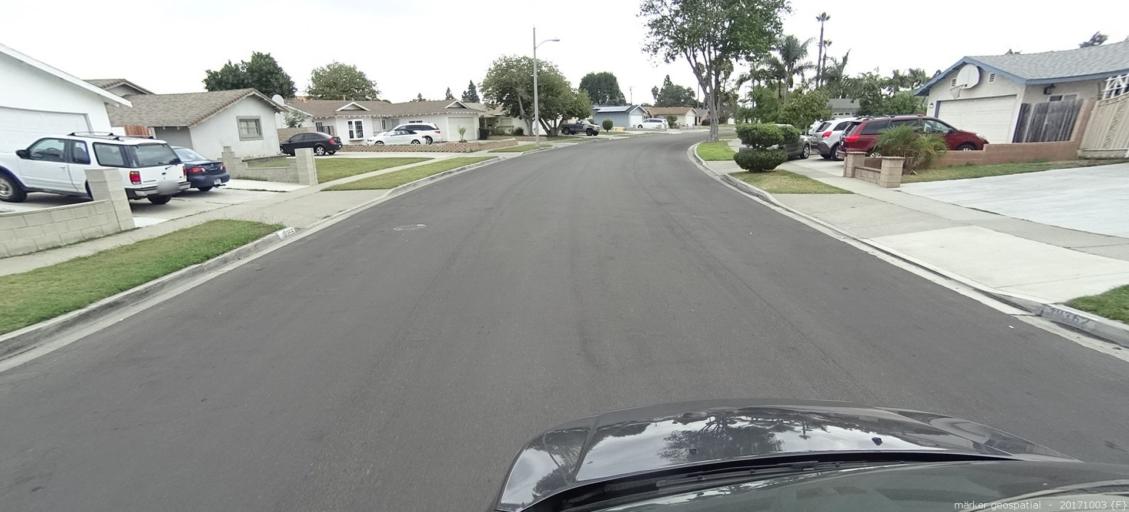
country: US
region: California
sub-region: Orange County
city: Garden Grove
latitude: 33.7626
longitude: -117.9485
